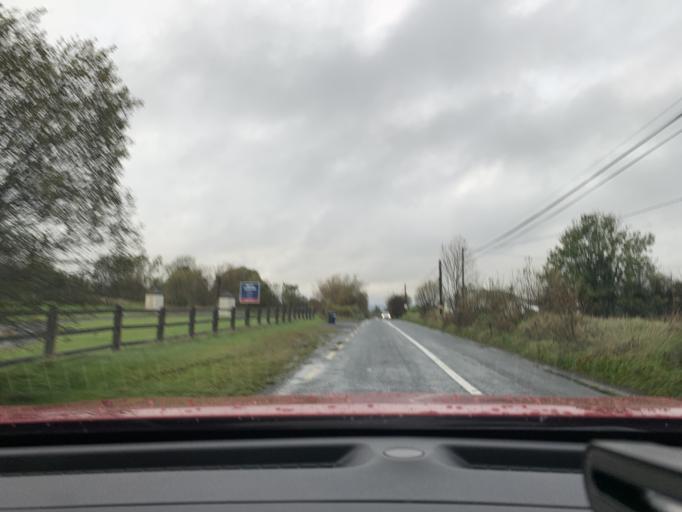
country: IE
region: Connaught
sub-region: Sligo
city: Ballymote
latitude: 54.0729
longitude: -8.5103
